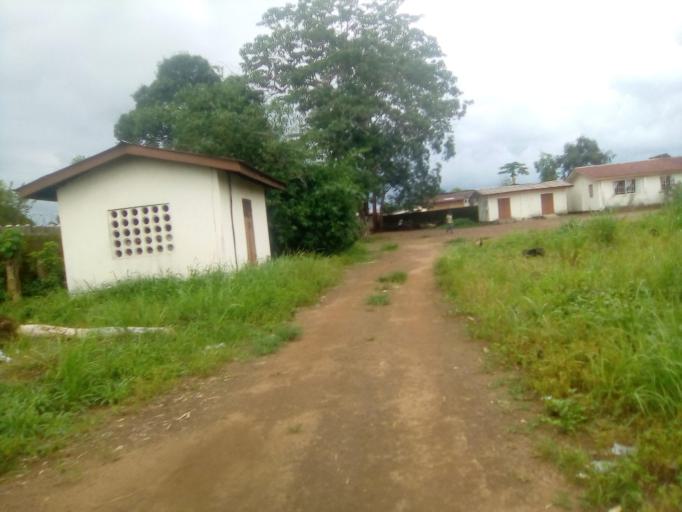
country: SL
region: Southern Province
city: Moyamba
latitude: 8.1487
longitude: -12.4337
